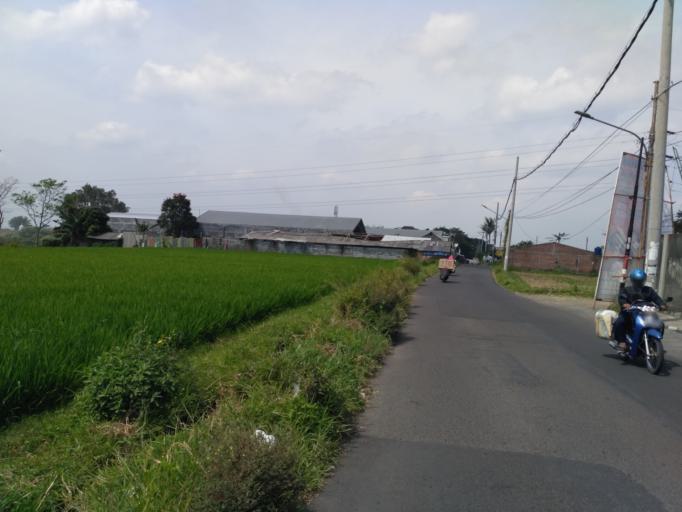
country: ID
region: East Java
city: Malang
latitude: -7.9231
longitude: 112.6023
